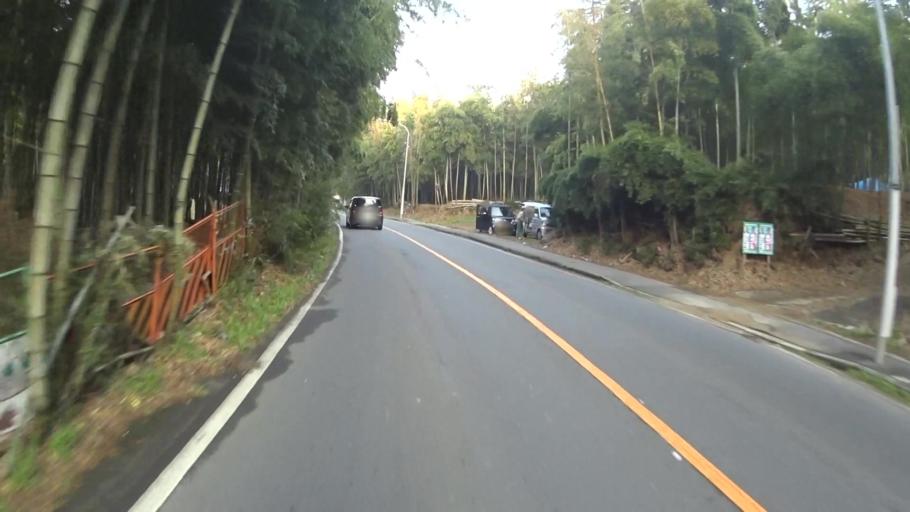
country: JP
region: Kyoto
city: Muko
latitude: 34.9527
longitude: 135.6897
